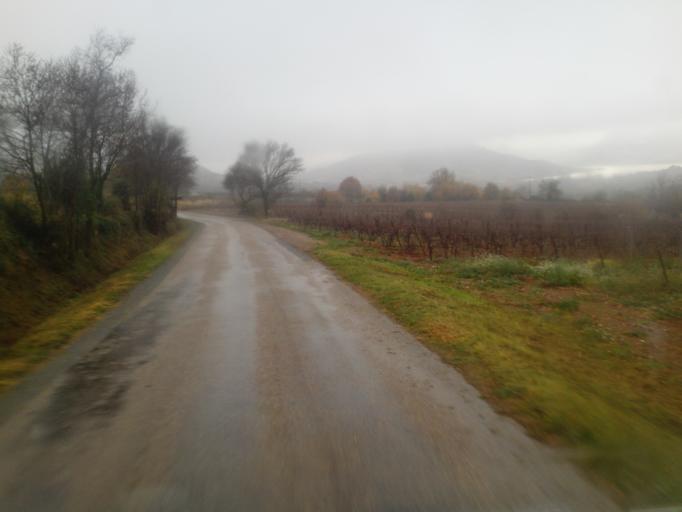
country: FR
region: Languedoc-Roussillon
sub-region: Departement de l'Herault
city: Nebian
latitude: 43.6370
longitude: 3.3661
